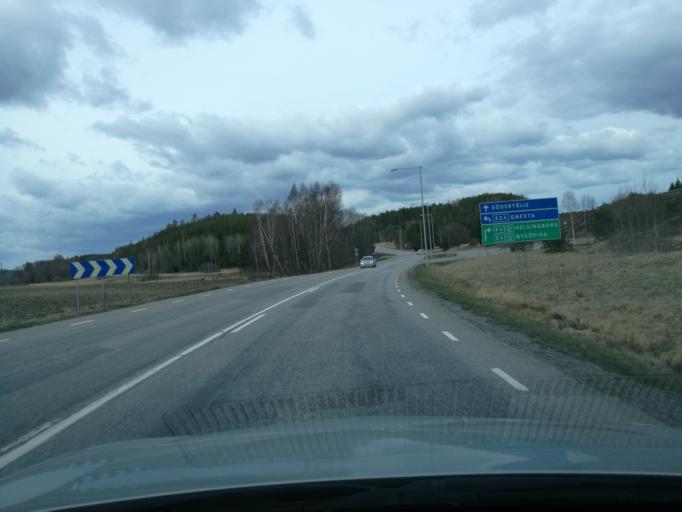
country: SE
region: Soedermanland
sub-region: Gnesta Kommun
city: Gnesta
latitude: 58.9084
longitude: 17.3269
